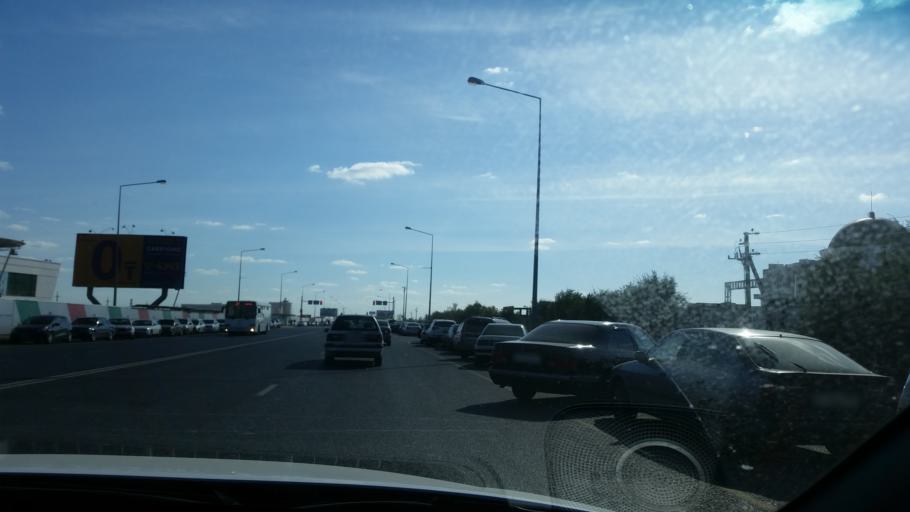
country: KZ
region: Astana Qalasy
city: Astana
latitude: 51.0915
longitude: 71.4034
